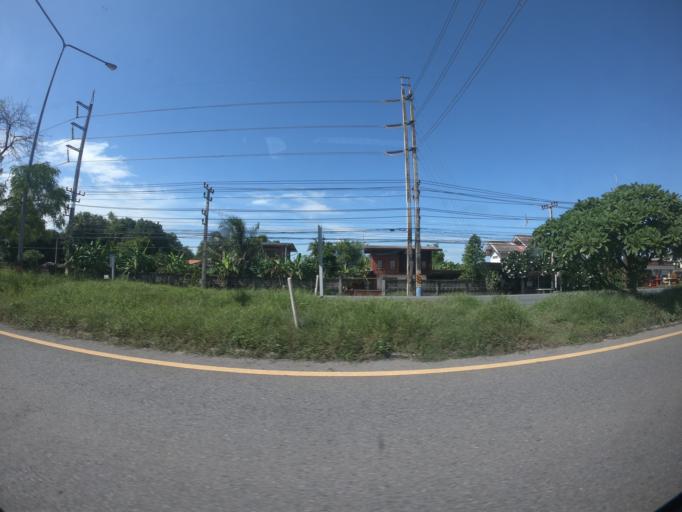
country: TH
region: Nakhon Nayok
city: Ban Na
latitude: 14.2404
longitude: 101.1396
